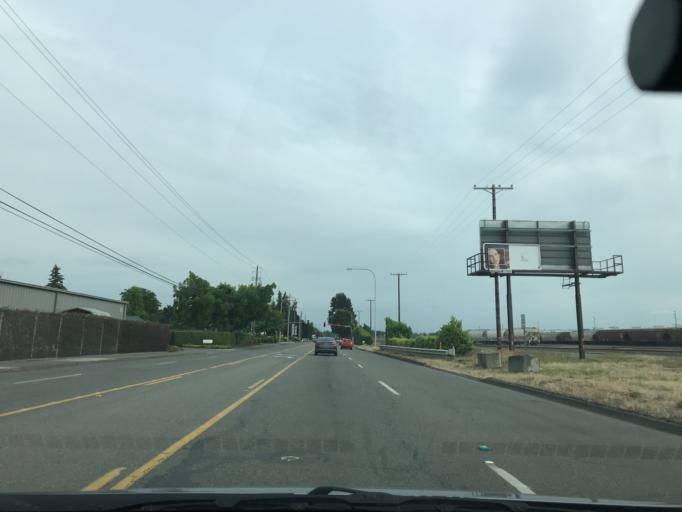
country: US
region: Washington
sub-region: King County
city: Auburn
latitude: 47.2843
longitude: -122.2289
